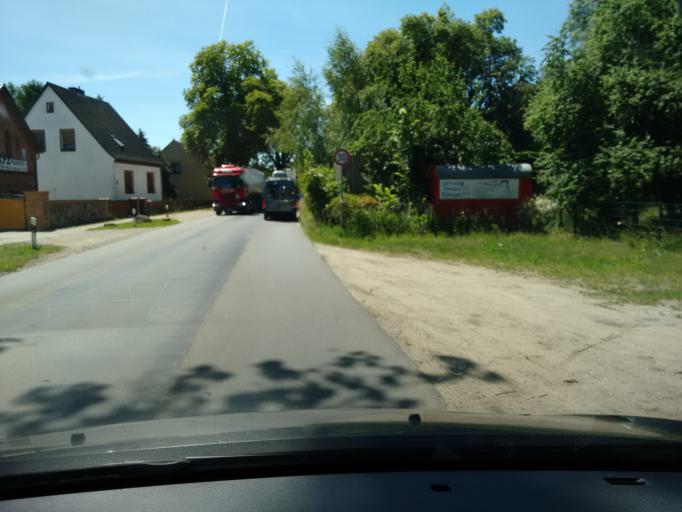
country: DE
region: Brandenburg
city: Rietz Neuendorf
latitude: 52.2669
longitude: 14.1636
